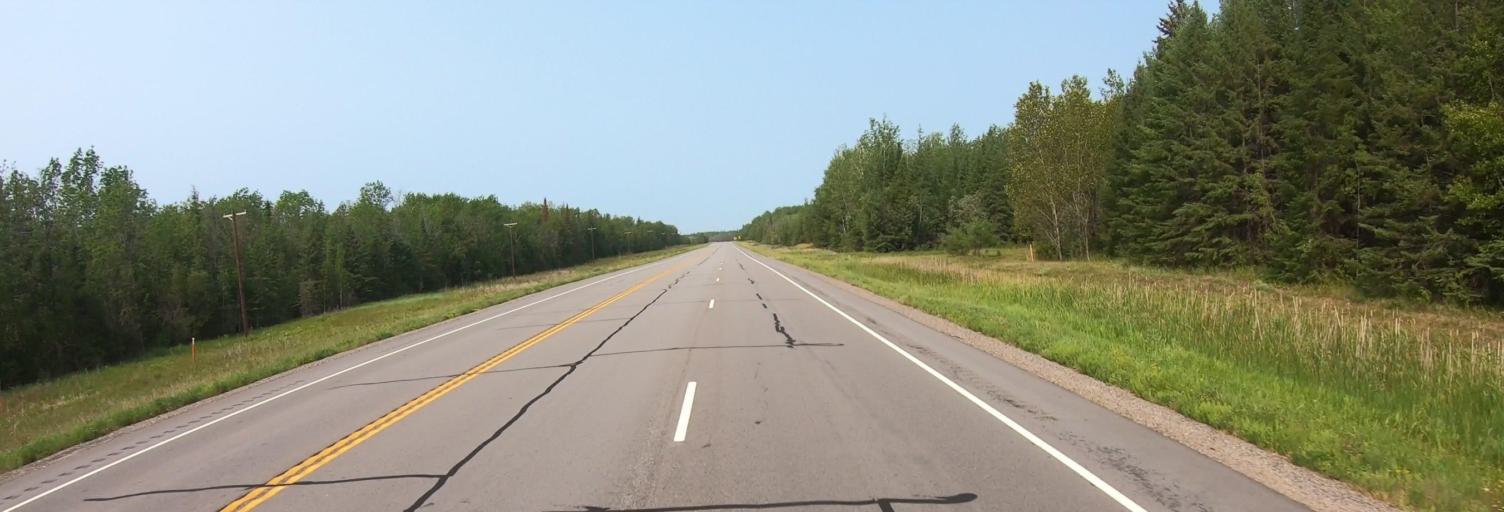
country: CA
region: Ontario
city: Fort Frances
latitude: 48.4043
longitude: -93.0309
